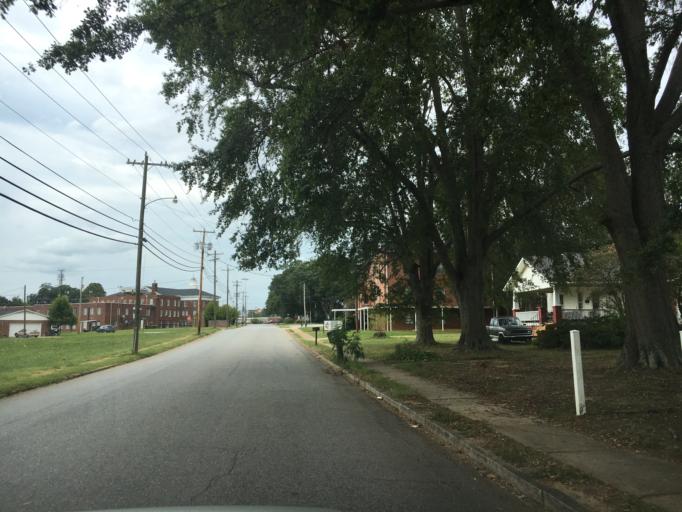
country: US
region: South Carolina
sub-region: Greenville County
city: Greer
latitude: 34.9336
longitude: -82.2203
